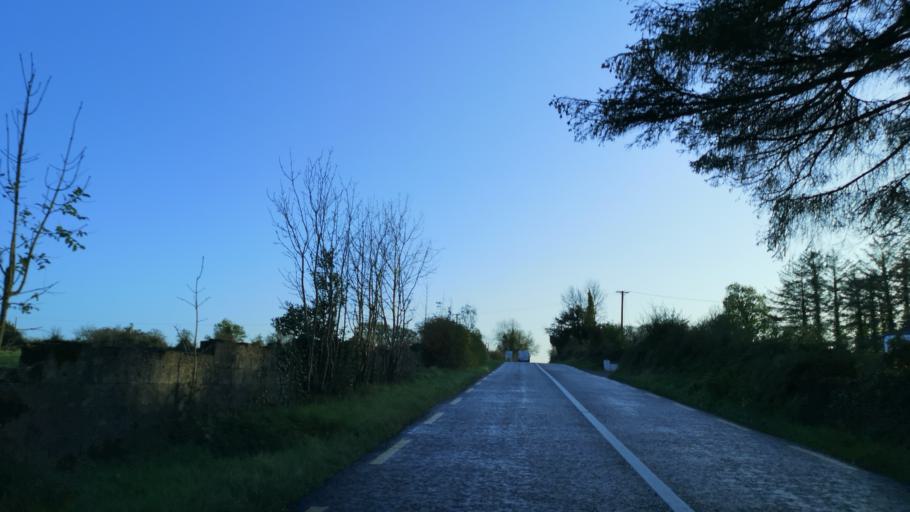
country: IE
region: Connaught
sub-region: Roscommon
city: Castlerea
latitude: 53.7262
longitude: -8.5566
